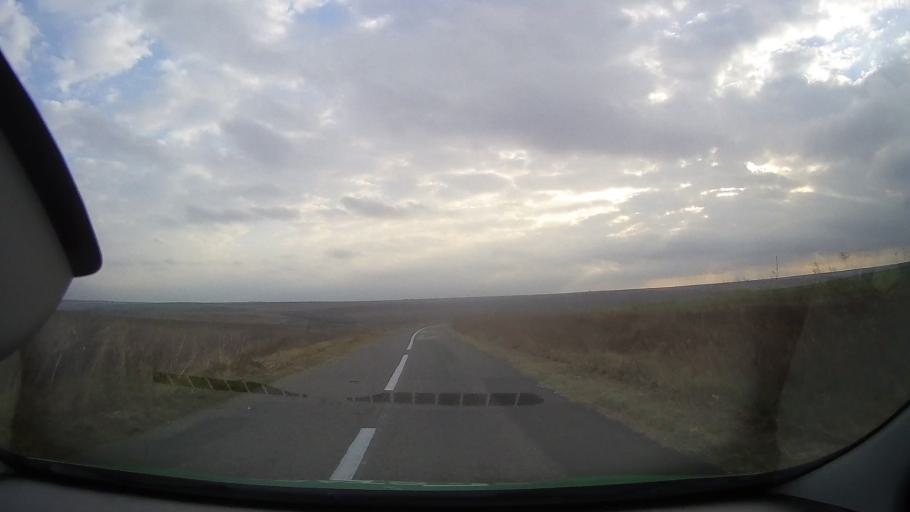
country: RO
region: Constanta
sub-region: Comuna Deleni
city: Pietreni
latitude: 44.1215
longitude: 28.1043
